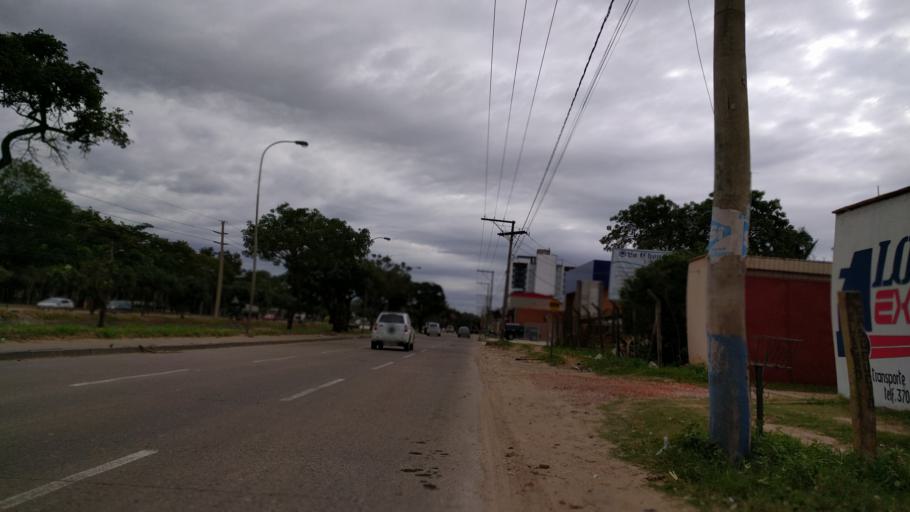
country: BO
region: Santa Cruz
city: Santa Cruz de la Sierra
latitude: -17.7823
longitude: -63.2163
